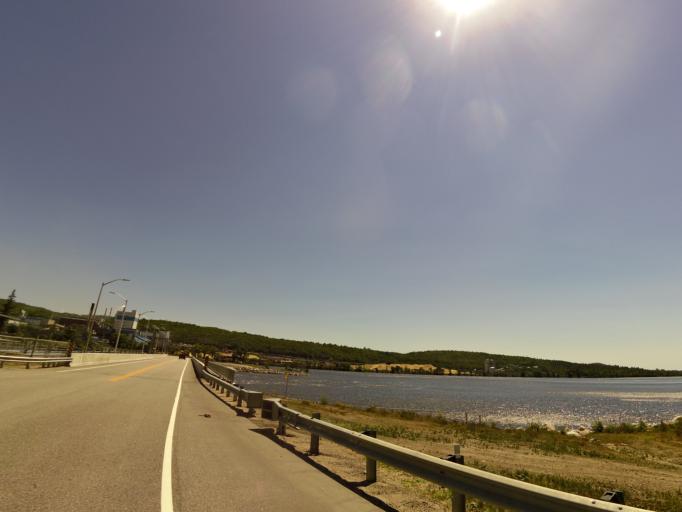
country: CA
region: Quebec
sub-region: Abitibi-Temiscamingue
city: Temiscaming
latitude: 46.7080
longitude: -79.1042
